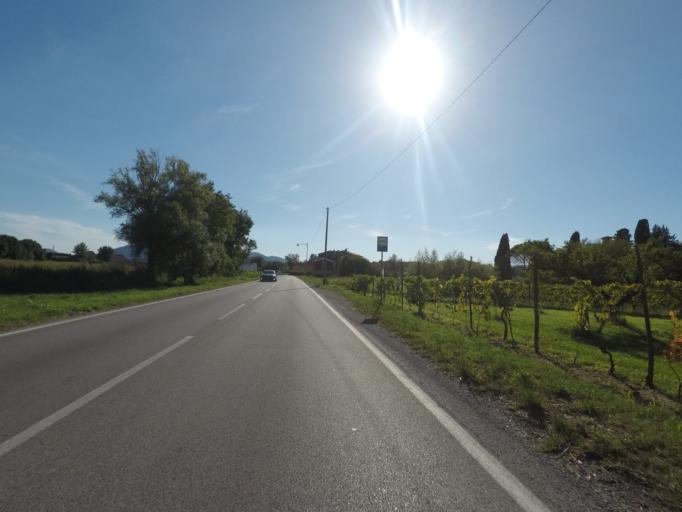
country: IT
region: Tuscany
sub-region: Provincia di Lucca
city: Lucca
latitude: 43.8692
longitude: 10.5137
